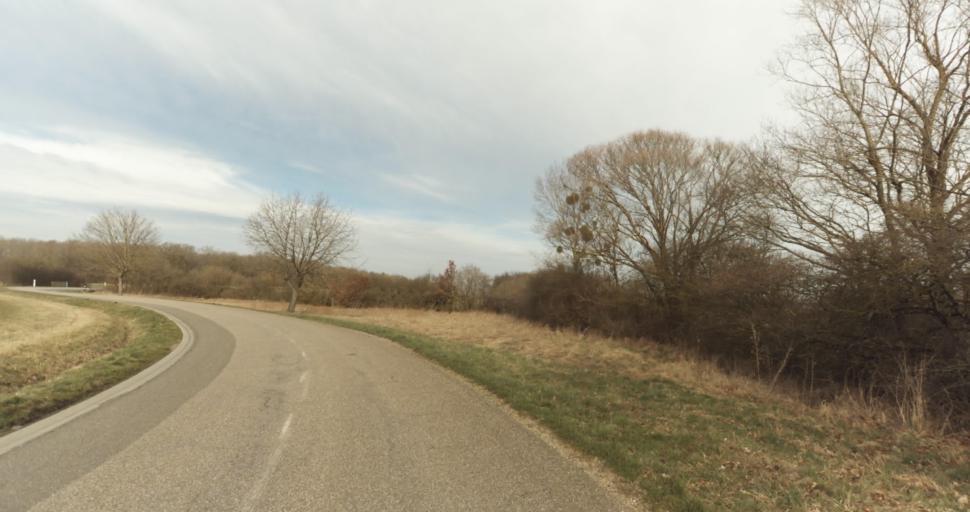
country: FR
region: Lorraine
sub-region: Departement de Meurthe-et-Moselle
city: Jarny
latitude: 49.1311
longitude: 5.8550
